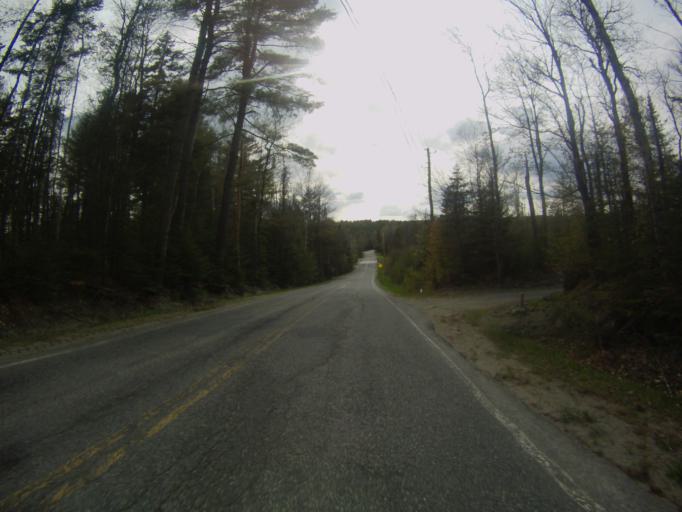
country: US
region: New York
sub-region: Warren County
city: Warrensburg
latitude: 43.8398
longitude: -73.8513
